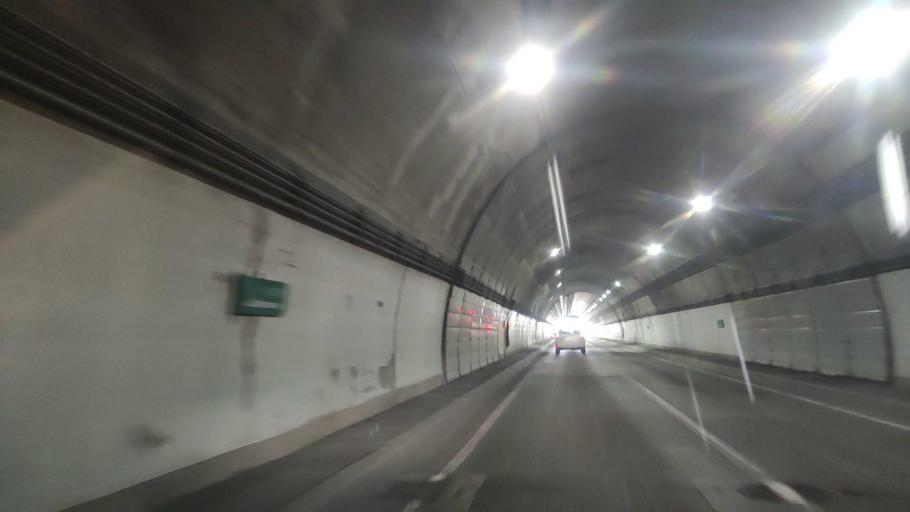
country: JP
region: Hokkaido
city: Ishikari
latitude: 43.4399
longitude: 141.4153
